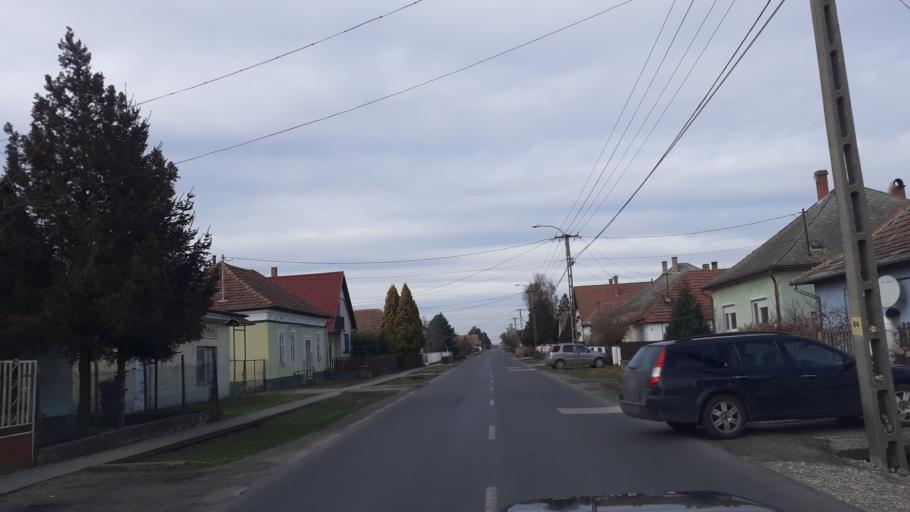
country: HU
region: Fejer
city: Sarbogard
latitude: 46.8977
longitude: 18.6059
